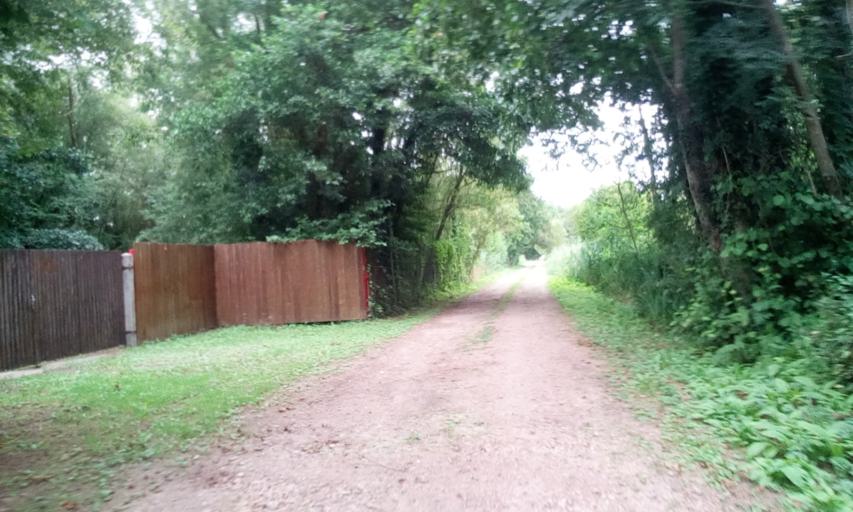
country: FR
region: Lower Normandy
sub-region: Departement du Calvados
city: Bellengreville
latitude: 49.1144
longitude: -0.2210
